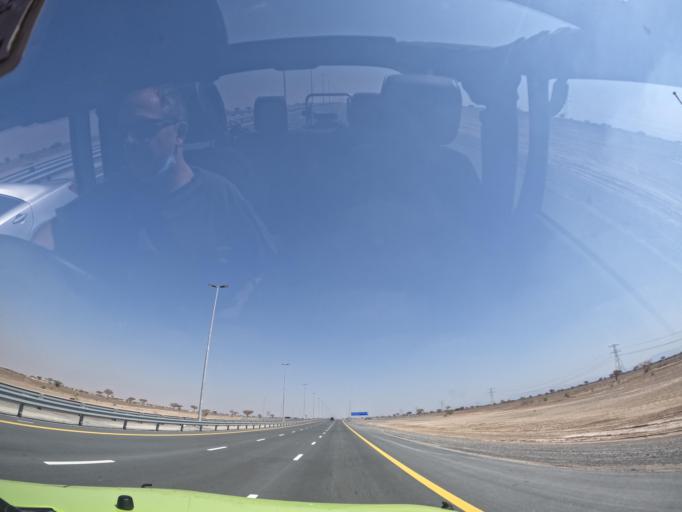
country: AE
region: Ash Shariqah
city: Adh Dhayd
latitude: 24.9502
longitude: 55.8340
